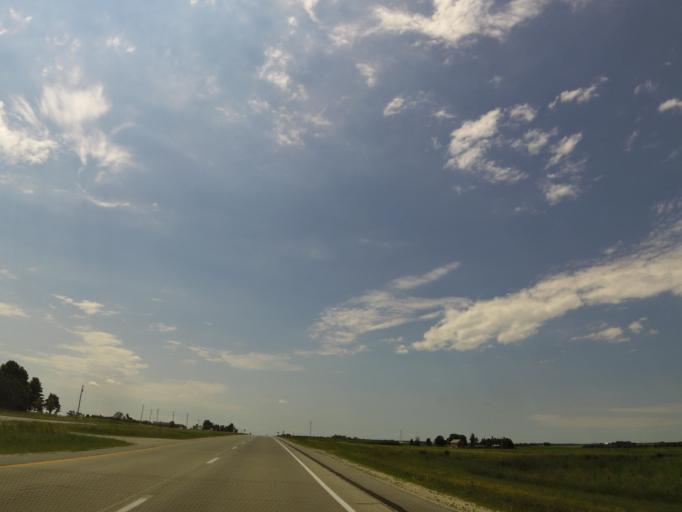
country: US
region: Iowa
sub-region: Bremer County
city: Denver
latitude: 42.7478
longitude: -92.3378
